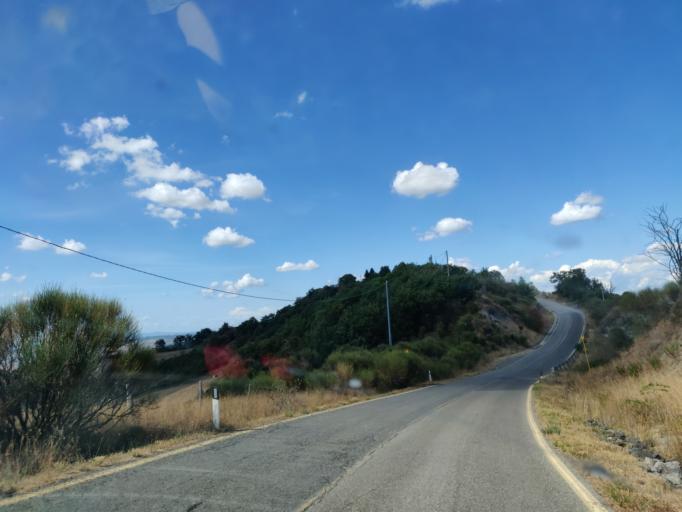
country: IT
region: Tuscany
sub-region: Provincia di Siena
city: Radicofani
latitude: 42.9560
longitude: 11.7266
